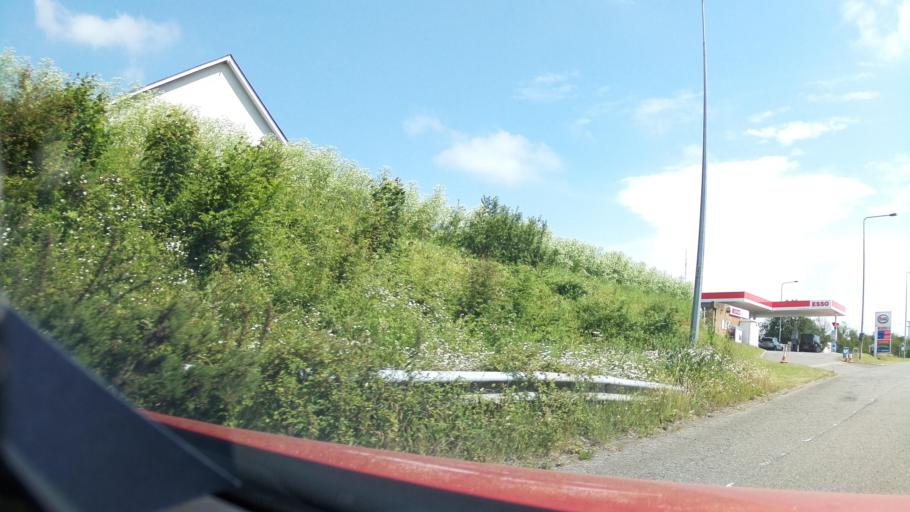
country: GB
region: Wales
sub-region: Vale of Glamorgan
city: Cowbridge
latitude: 51.4599
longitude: -3.4233
